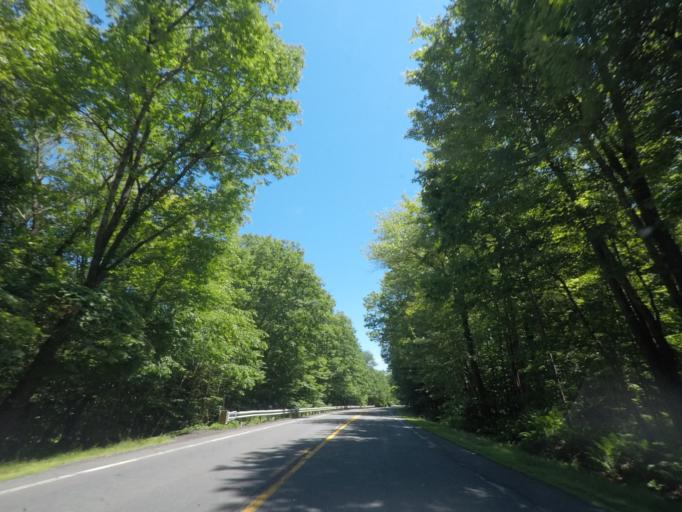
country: US
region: Massachusetts
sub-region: Hampshire County
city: Westhampton
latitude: 42.2469
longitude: -72.9218
